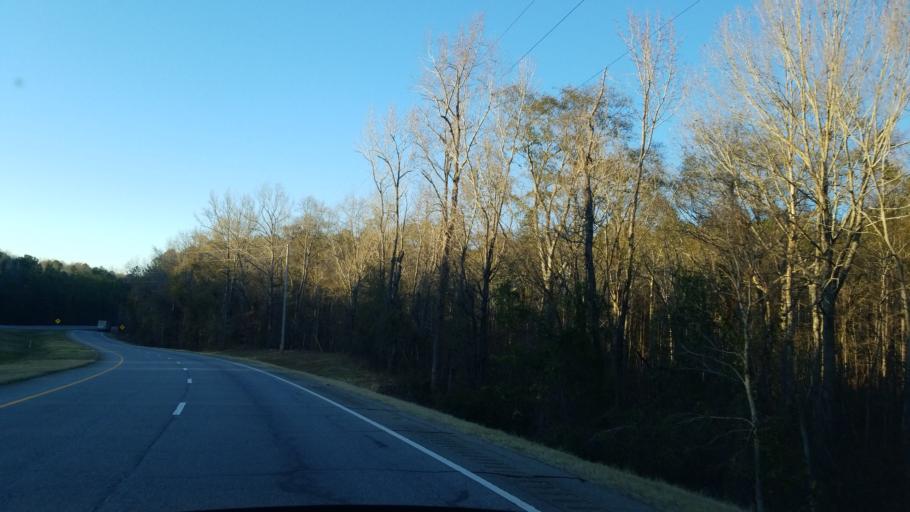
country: US
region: Georgia
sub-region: Chattahoochee County
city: Cusseta
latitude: 32.2408
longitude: -84.7147
